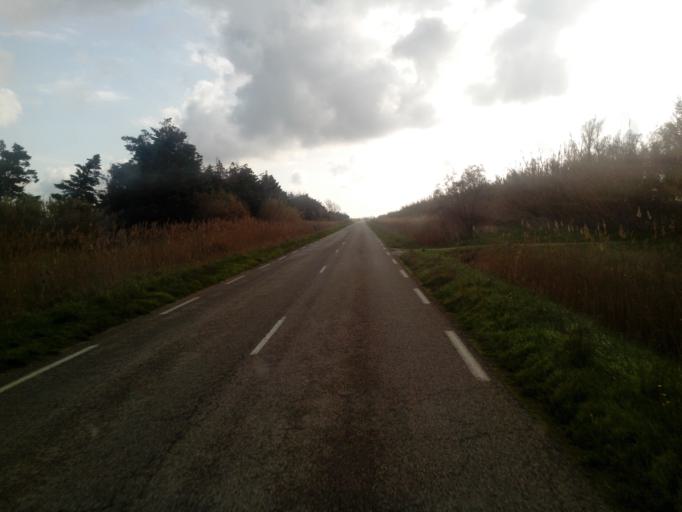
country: FR
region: Provence-Alpes-Cote d'Azur
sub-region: Departement des Bouches-du-Rhone
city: Port-Saint-Louis-du-Rhone
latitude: 43.4999
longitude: 4.7079
